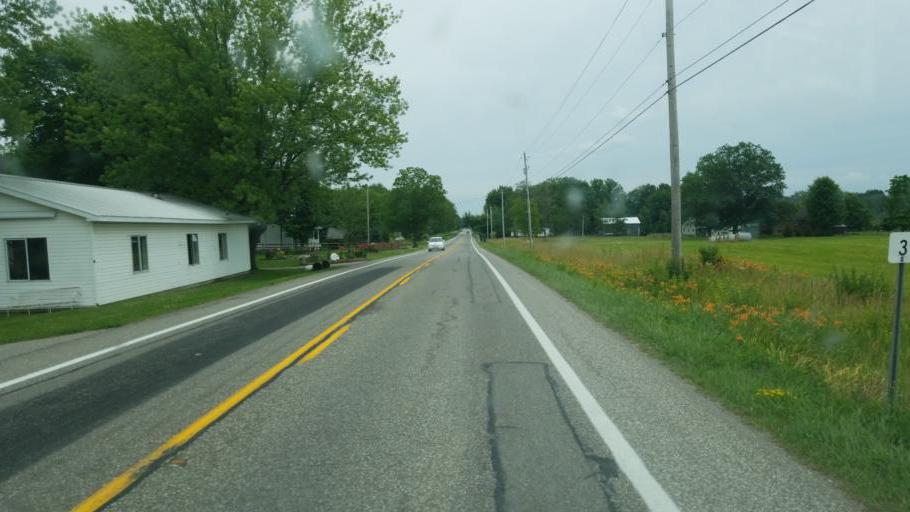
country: US
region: Ohio
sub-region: Ashtabula County
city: Orwell
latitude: 41.4582
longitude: -80.9456
